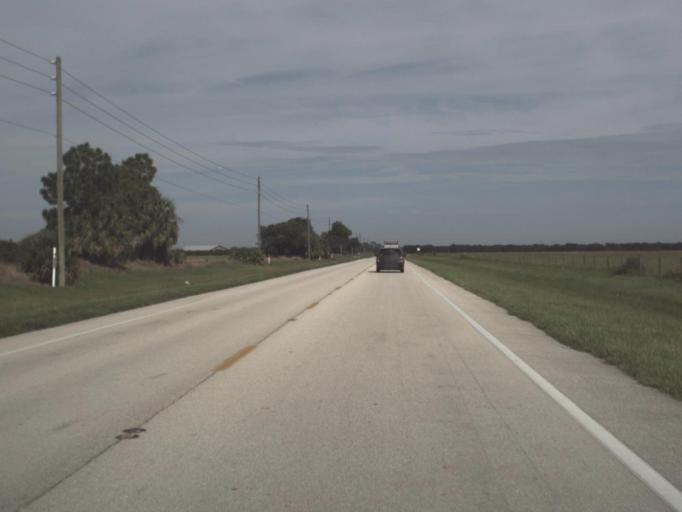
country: US
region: Florida
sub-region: DeSoto County
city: Nocatee
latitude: 27.0373
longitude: -81.7741
